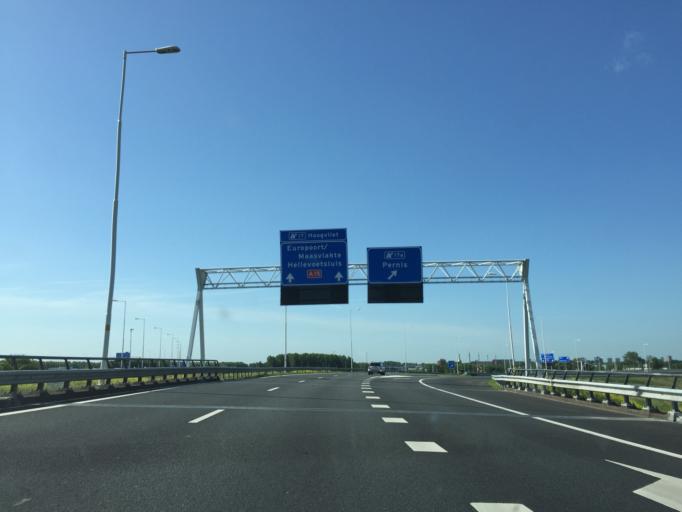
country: NL
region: South Holland
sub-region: Gemeente Schiedam
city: Schiedam
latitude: 51.8777
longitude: 4.3843
